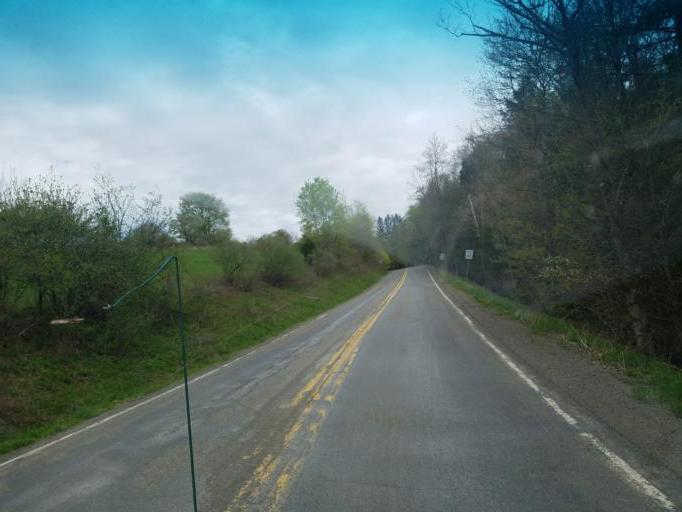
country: US
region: Pennsylvania
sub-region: Tioga County
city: Wellsboro
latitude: 41.7002
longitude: -77.4392
